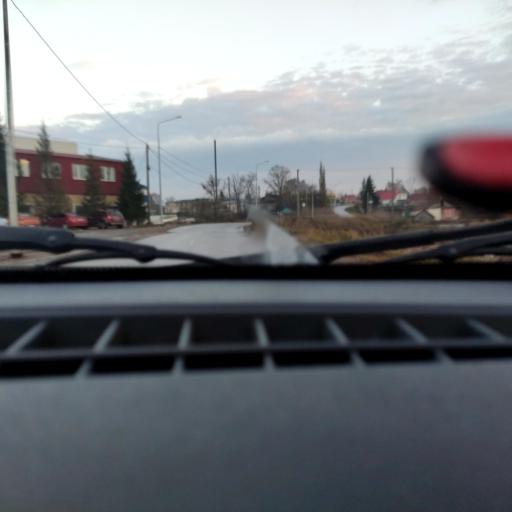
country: RU
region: Bashkortostan
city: Avdon
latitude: 54.5007
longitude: 55.8814
